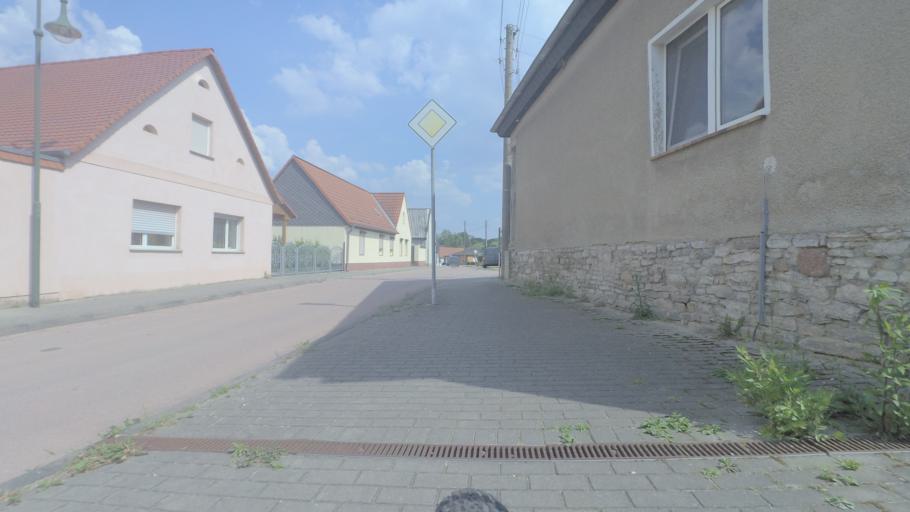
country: DE
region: Saxony-Anhalt
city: Koethen
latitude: 51.7622
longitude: 11.9300
